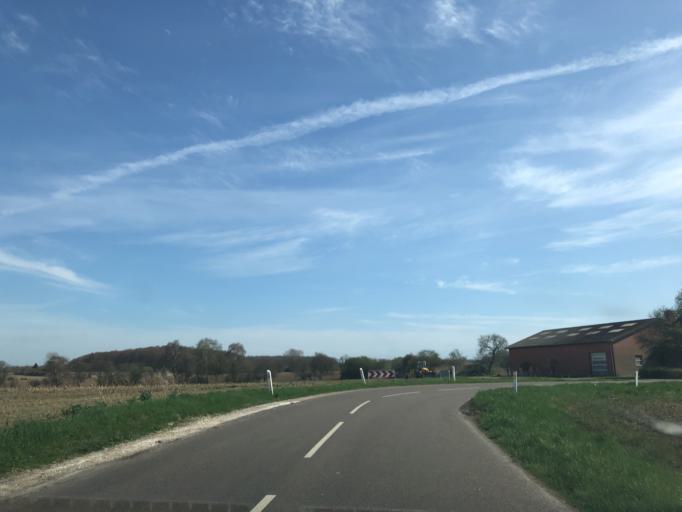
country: DK
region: Zealand
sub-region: Faxe Kommune
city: Ronnede
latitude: 55.2958
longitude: 12.0703
